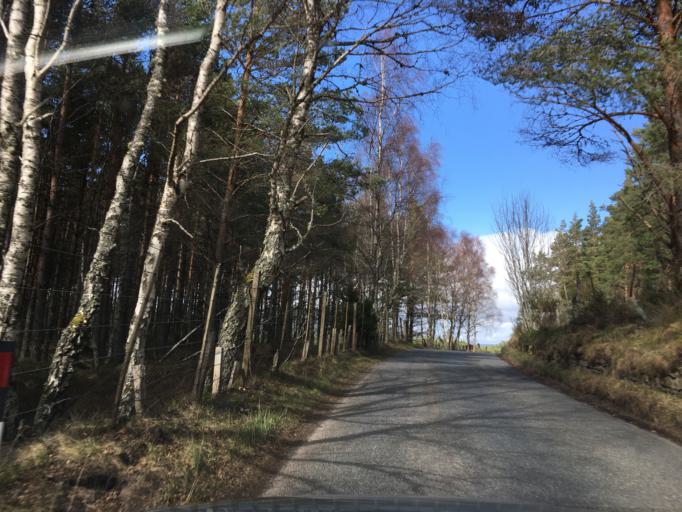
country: GB
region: Scotland
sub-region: Highland
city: Aviemore
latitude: 57.1992
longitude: -3.7981
